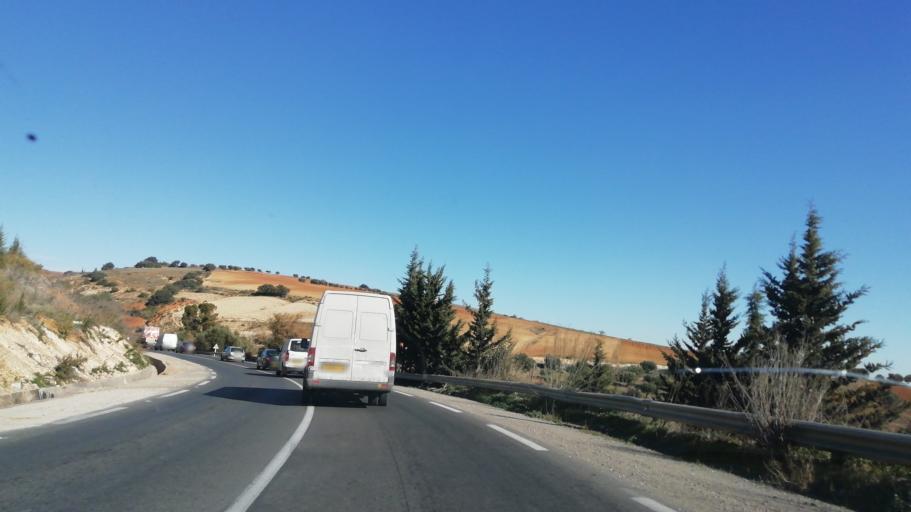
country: DZ
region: Mascara
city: Mascara
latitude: 35.4993
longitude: 0.2670
